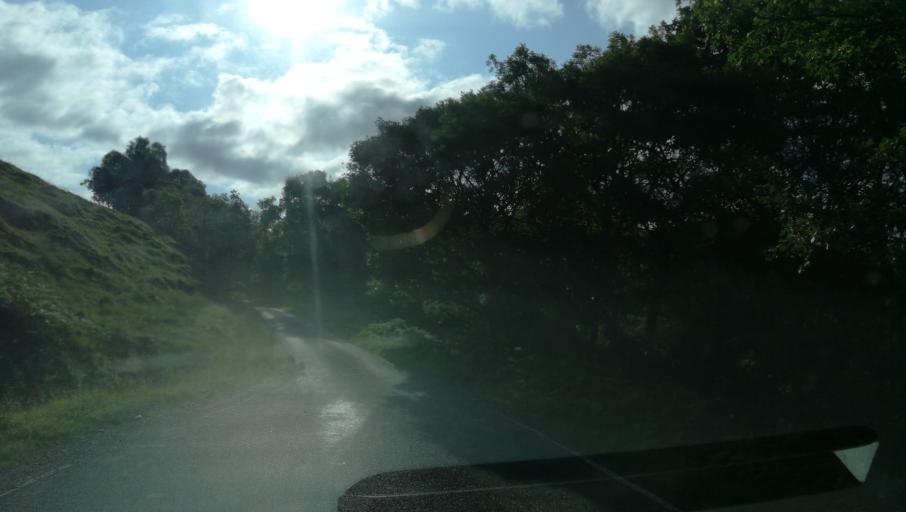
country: GB
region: Scotland
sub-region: Argyll and Bute
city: Isle Of Mull
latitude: 56.6799
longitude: -5.8554
